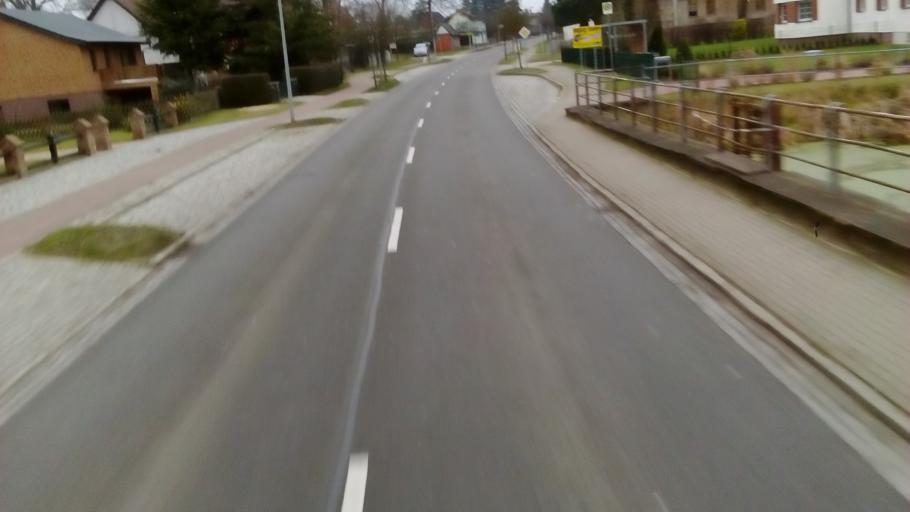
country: DE
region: Mecklenburg-Vorpommern
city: Viereck
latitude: 53.4996
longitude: 14.0592
